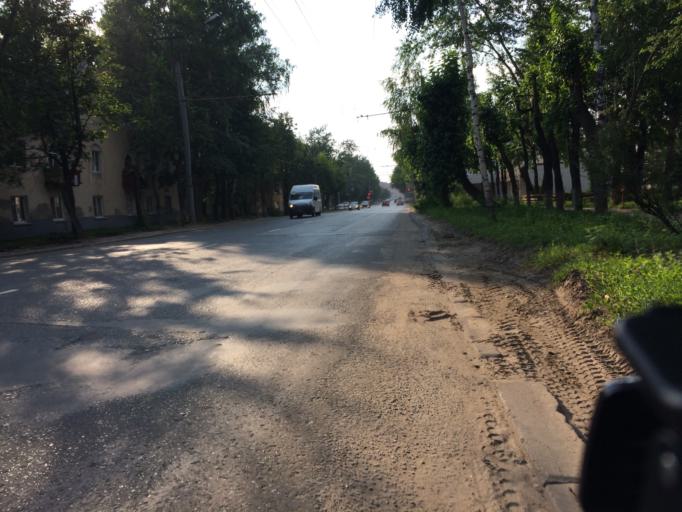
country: RU
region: Mariy-El
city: Yoshkar-Ola
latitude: 56.6337
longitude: 47.9447
